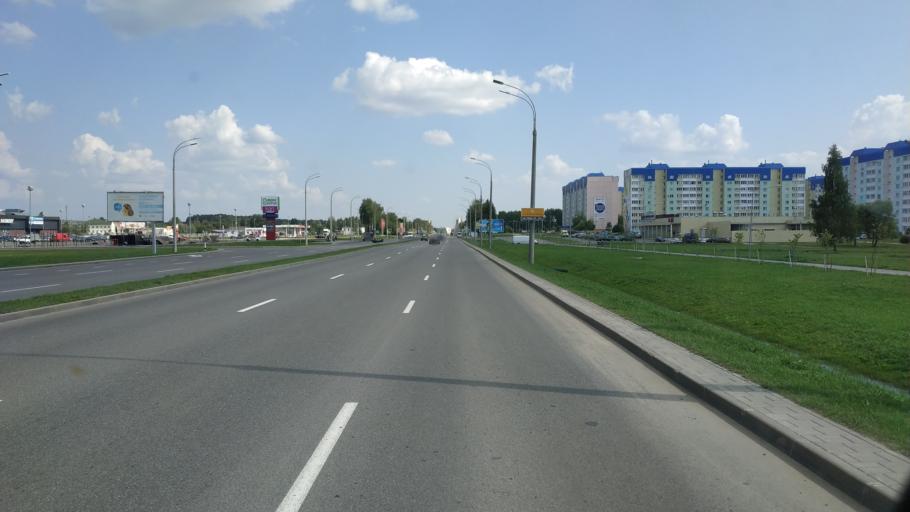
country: BY
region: Mogilev
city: Buynichy
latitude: 53.9351
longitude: 30.2530
